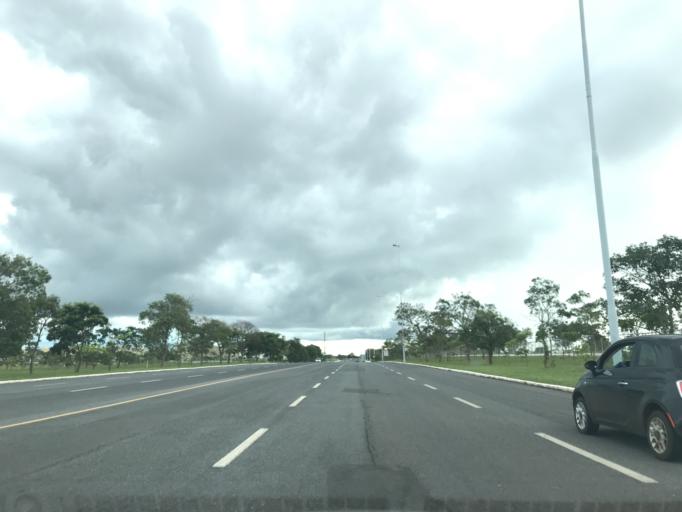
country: BR
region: Federal District
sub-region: Brasilia
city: Brasilia
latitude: -15.7670
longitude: -47.9180
